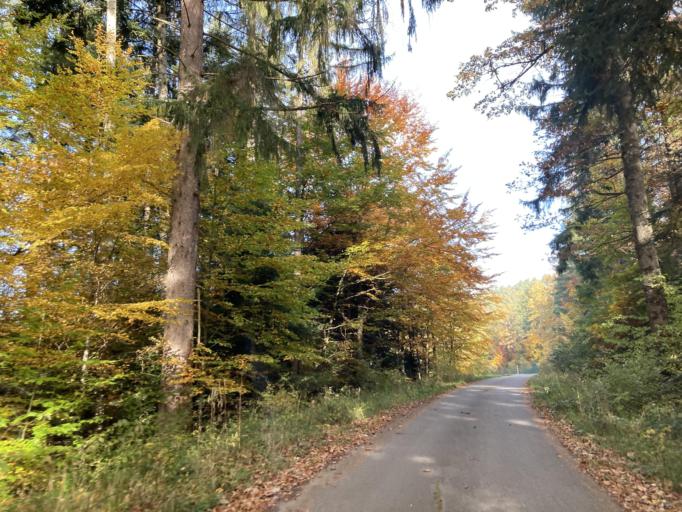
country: DE
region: Baden-Wuerttemberg
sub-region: Tuebingen Region
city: Bodelshausen
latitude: 48.4094
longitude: 8.9601
